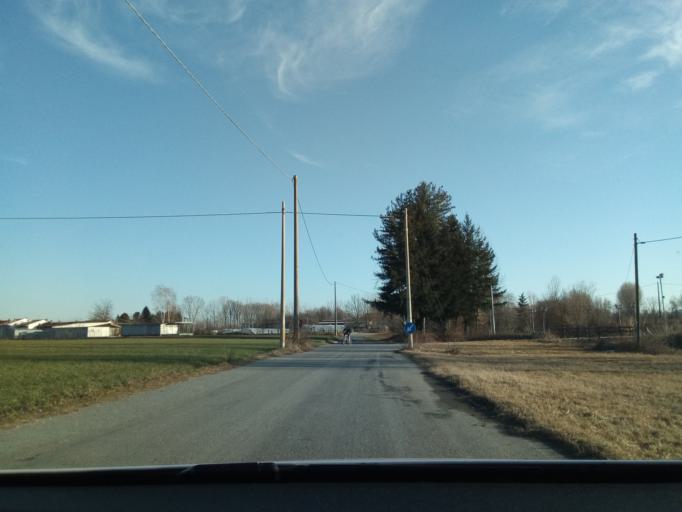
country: IT
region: Piedmont
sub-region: Provincia di Torino
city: Bollengo
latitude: 45.4640
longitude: 7.9306
